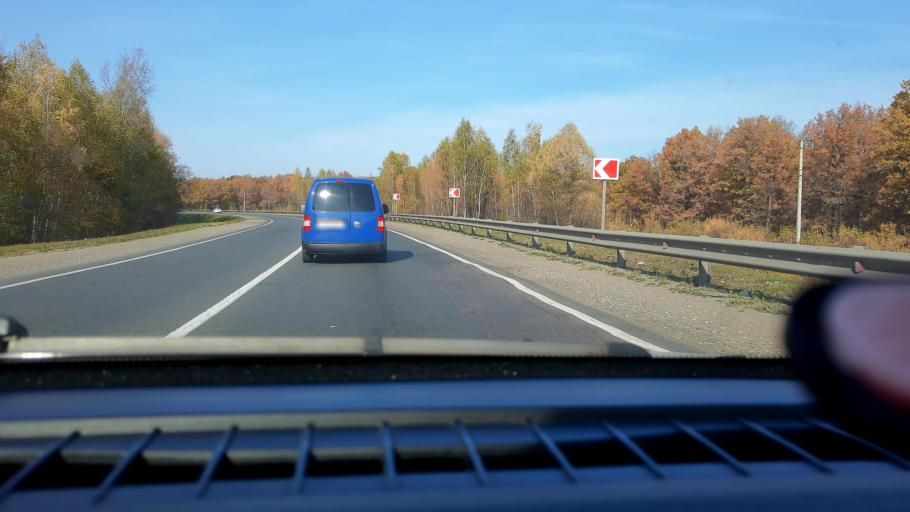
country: RU
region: Nizjnij Novgorod
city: Pamyat' Parizhskoy Kommuny
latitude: 56.0759
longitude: 44.3707
